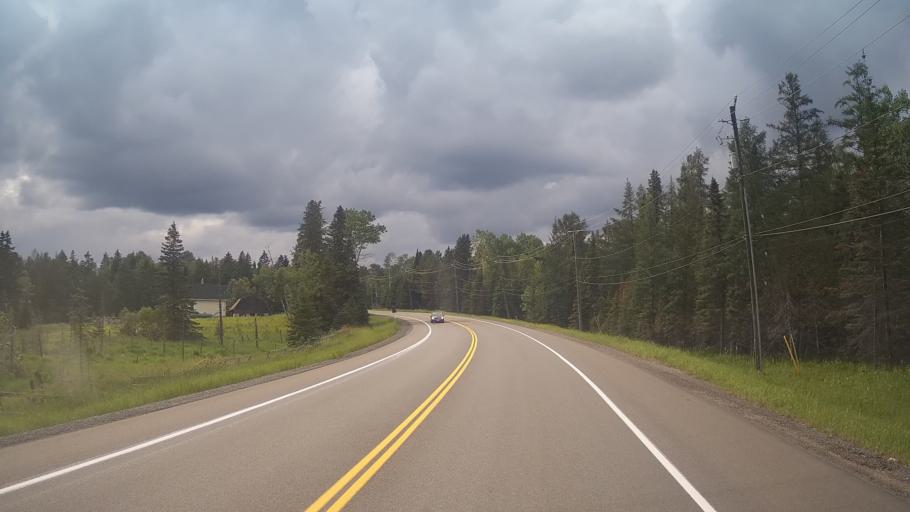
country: CA
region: Ontario
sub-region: Thunder Bay District
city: Thunder Bay
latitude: 48.4875
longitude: -89.3354
